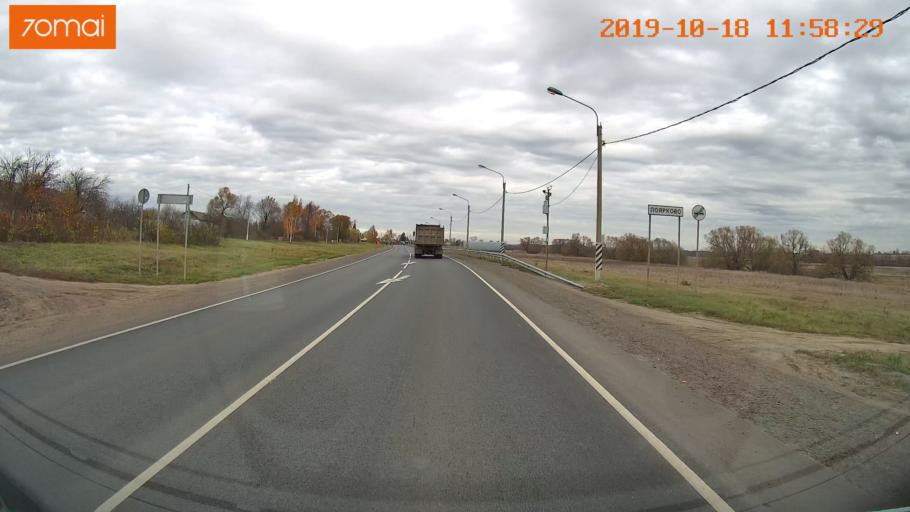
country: RU
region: Rjazan
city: Zakharovo
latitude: 54.2722
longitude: 39.1678
